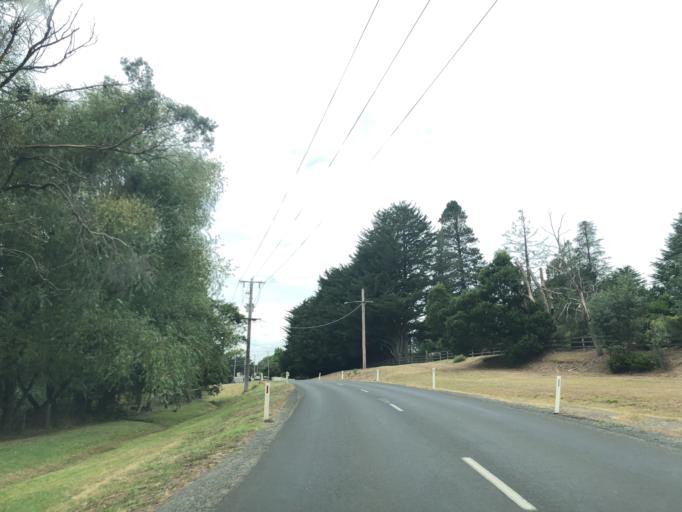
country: AU
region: Victoria
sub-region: Hume
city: Sunbury
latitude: -37.3622
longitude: 144.5228
